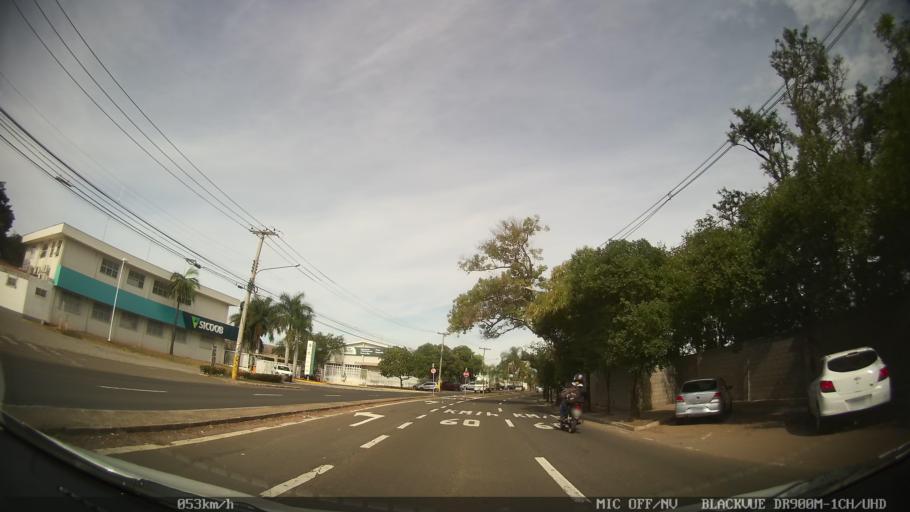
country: BR
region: Sao Paulo
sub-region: Piracicaba
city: Piracicaba
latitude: -22.7544
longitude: -47.6368
